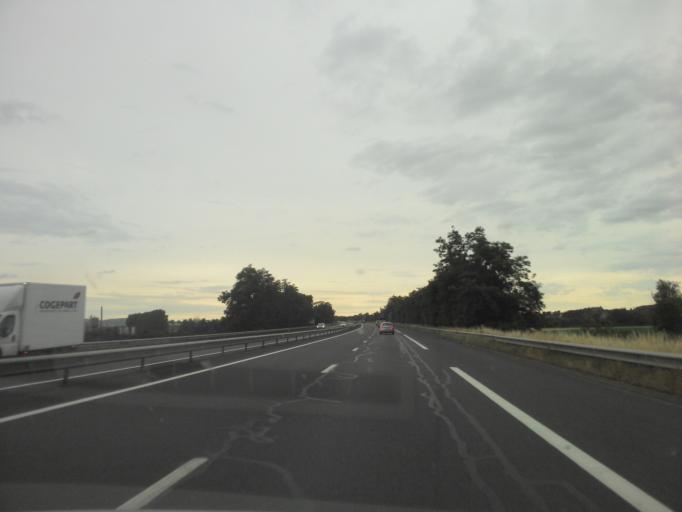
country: FR
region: Auvergne
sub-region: Departement du Puy-de-Dome
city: Riom
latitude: 45.9119
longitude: 3.1528
